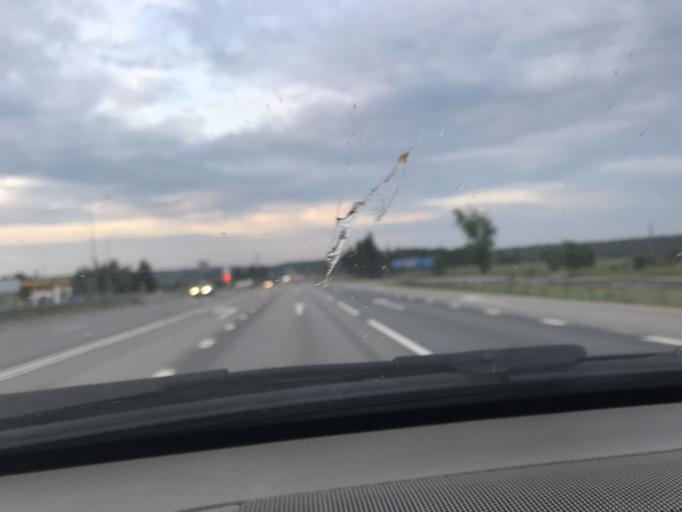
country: RU
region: Kaluga
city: Obninsk
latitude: 55.0416
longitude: 36.5958
